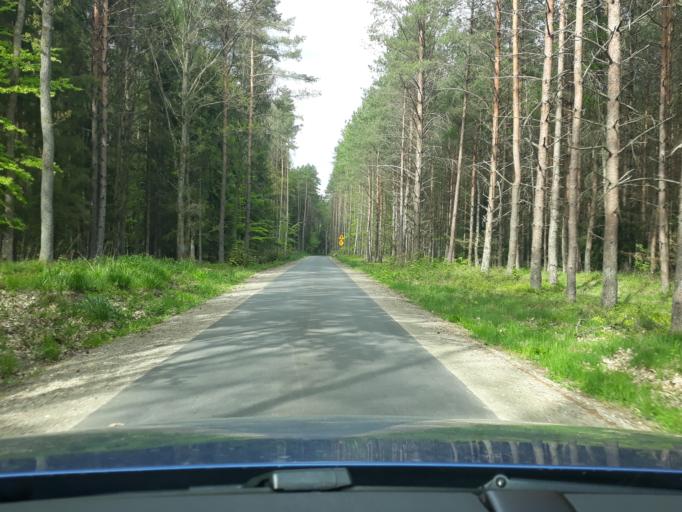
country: PL
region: Pomeranian Voivodeship
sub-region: Powiat czluchowski
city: Czluchow
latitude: 53.7399
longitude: 17.3467
